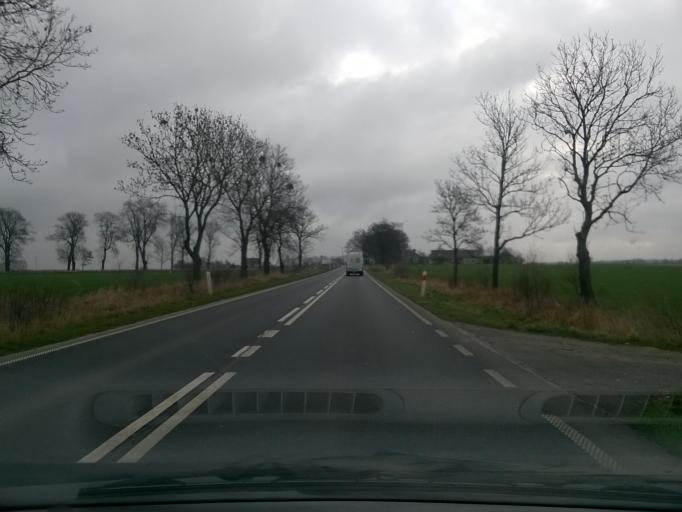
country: PL
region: Kujawsko-Pomorskie
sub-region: Powiat nakielski
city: Kcynia
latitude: 52.9880
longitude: 17.5393
